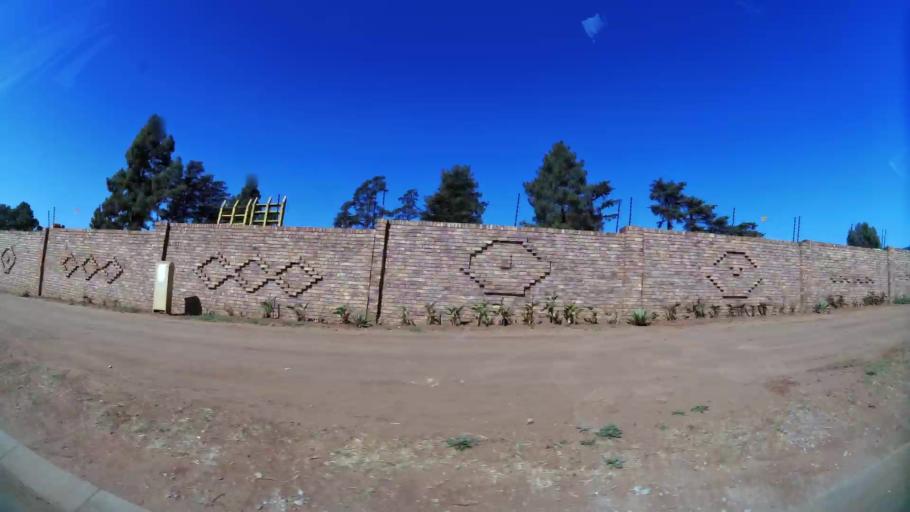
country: ZA
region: Gauteng
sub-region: City of Johannesburg Metropolitan Municipality
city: Modderfontein
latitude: -26.0744
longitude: 28.1903
